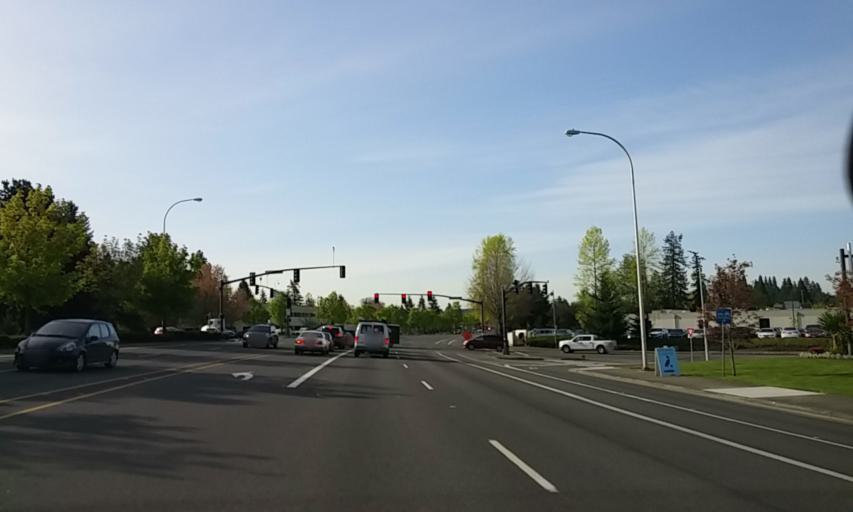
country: US
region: Oregon
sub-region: Washington County
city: Beaverton
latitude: 45.4951
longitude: -122.8268
